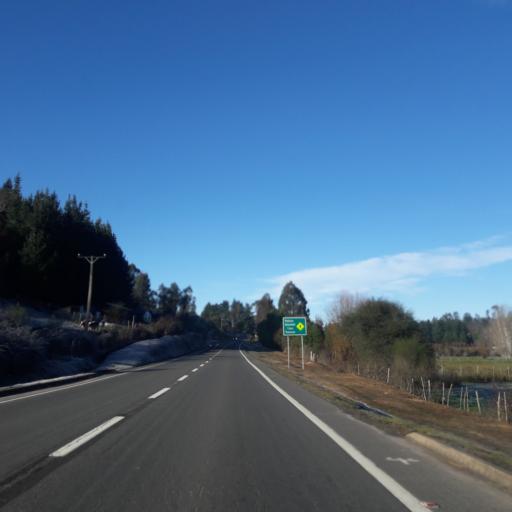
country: CL
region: Biobio
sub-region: Provincia de Biobio
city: La Laja
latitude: -37.3119
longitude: -72.9237
